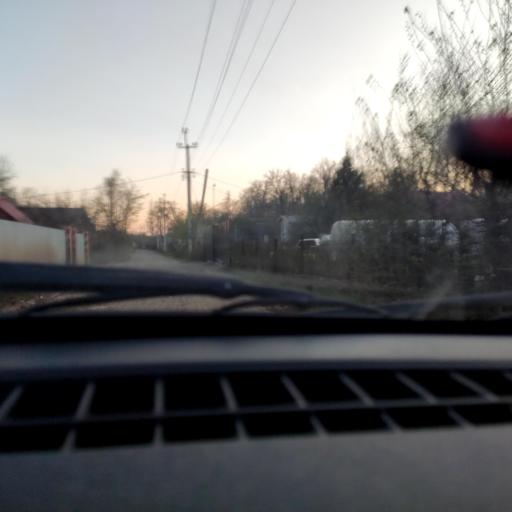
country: RU
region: Bashkortostan
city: Ufa
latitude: 54.6908
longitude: 55.8897
